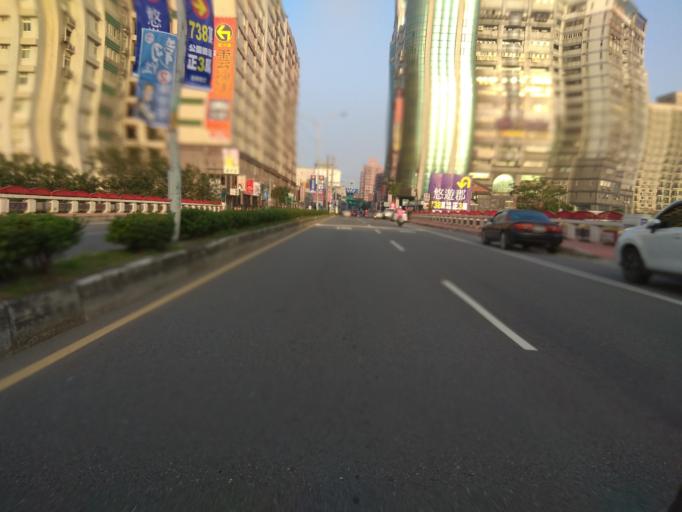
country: TW
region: Taiwan
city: Daxi
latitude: 24.9432
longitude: 121.2105
